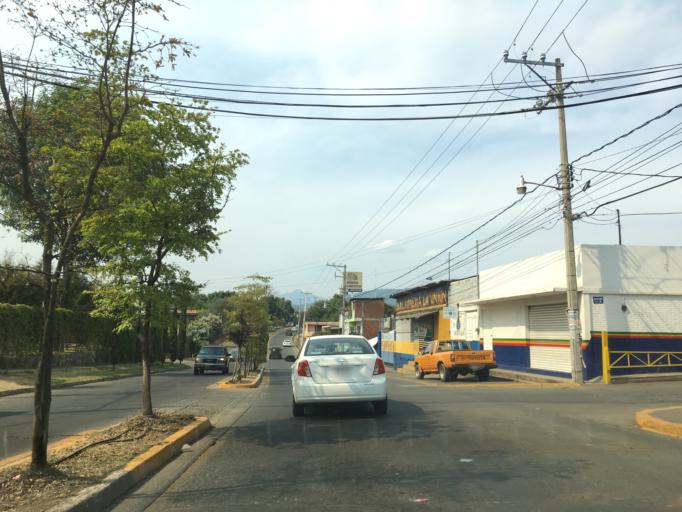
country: MX
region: Michoacan
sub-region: Uruapan
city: Uruapan
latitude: 19.3934
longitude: -102.0694
